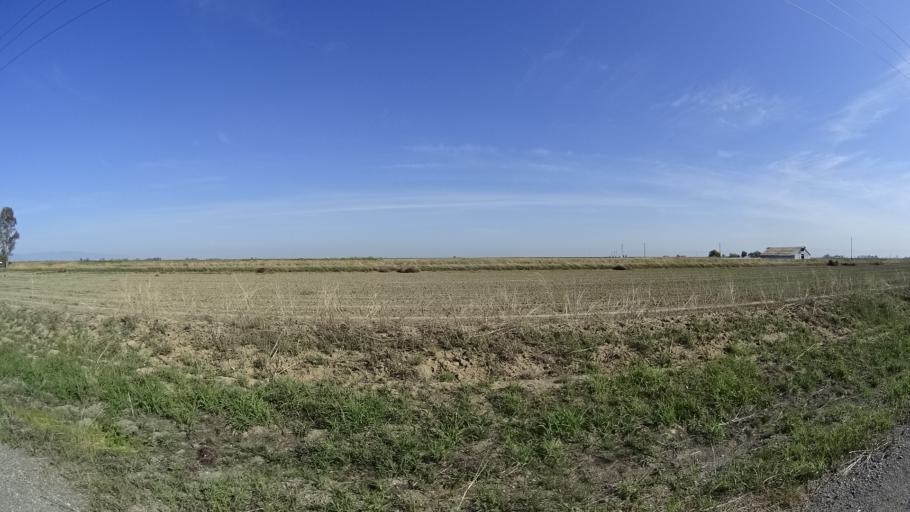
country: US
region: California
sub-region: Glenn County
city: Willows
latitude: 39.5531
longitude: -122.1392
